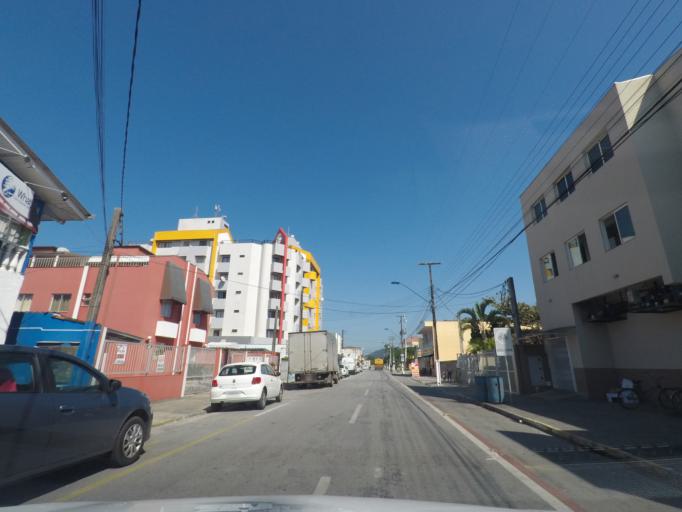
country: BR
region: Parana
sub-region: Guaratuba
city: Guaratuba
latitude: -25.8192
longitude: -48.5339
